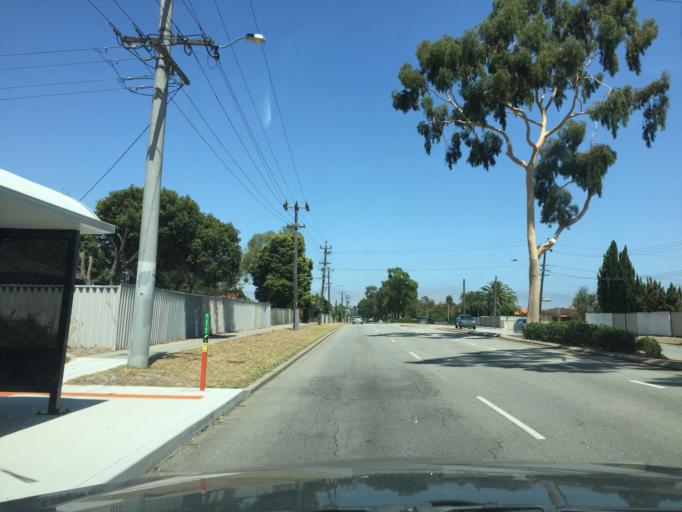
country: AU
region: Western Australia
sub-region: Canning
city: Ferndale
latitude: -32.0384
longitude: 115.9124
